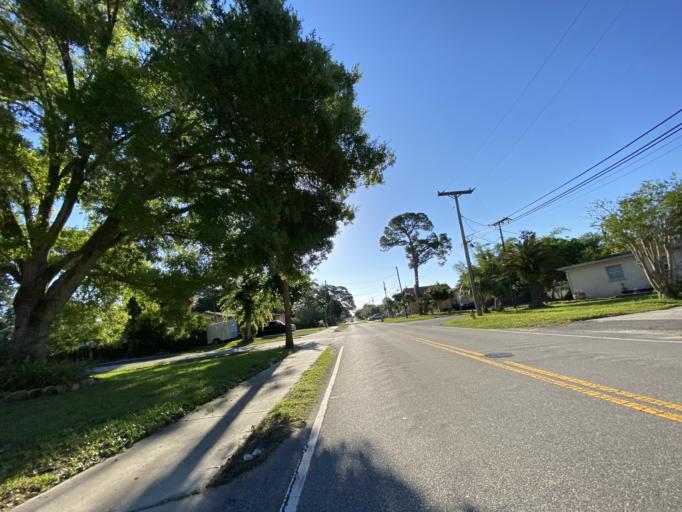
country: US
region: Florida
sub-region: Volusia County
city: Port Orange
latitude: 29.1463
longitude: -80.9931
